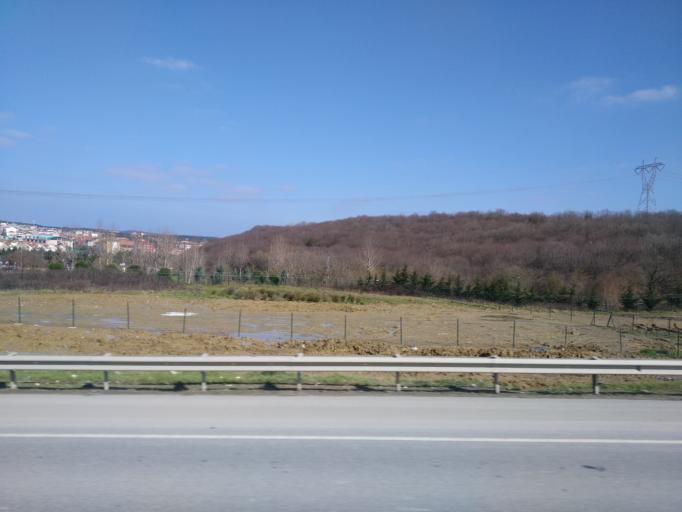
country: TR
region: Istanbul
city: Kemerburgaz
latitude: 41.1688
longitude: 28.8892
